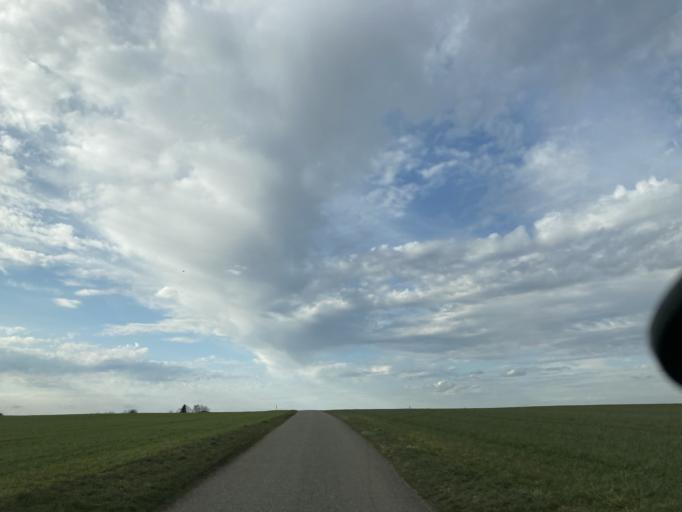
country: DE
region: Baden-Wuerttemberg
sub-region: Tuebingen Region
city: Nehren
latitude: 48.4397
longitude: 9.0696
